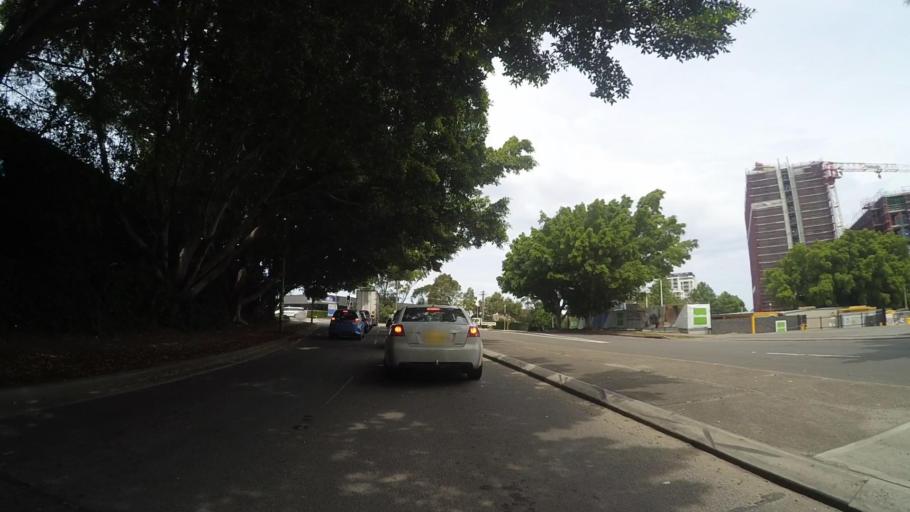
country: AU
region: New South Wales
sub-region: Botany Bay
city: Mascot
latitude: -33.9263
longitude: 151.1875
